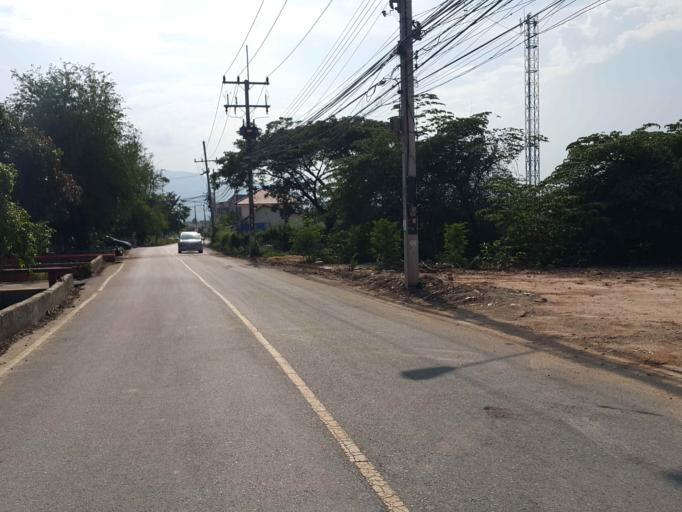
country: TH
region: Chiang Mai
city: San Sai
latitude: 18.8302
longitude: 99.0313
